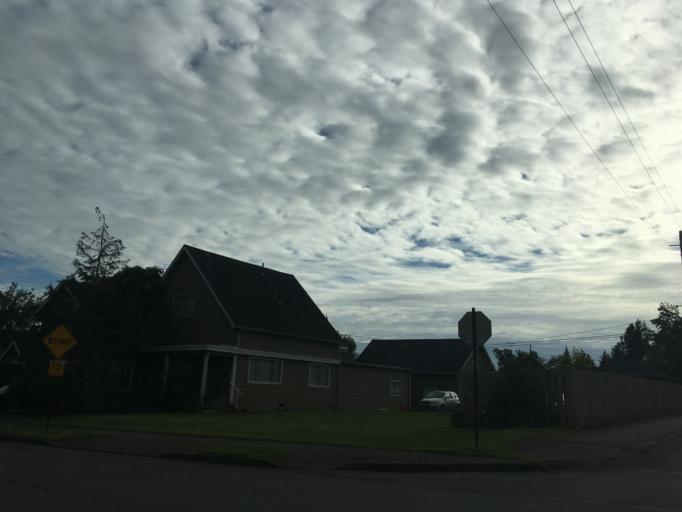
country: US
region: Washington
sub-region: Whatcom County
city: Bellingham
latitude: 48.7617
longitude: -122.4692
